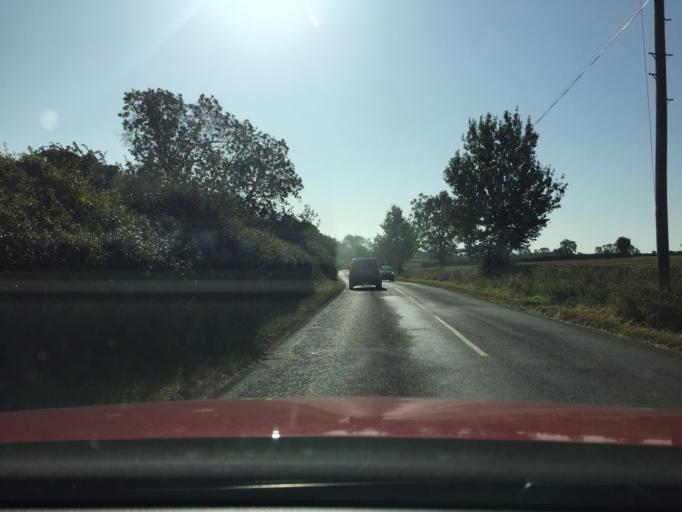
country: GB
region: England
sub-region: Leicestershire
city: Syston
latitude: 52.6703
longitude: -1.0288
